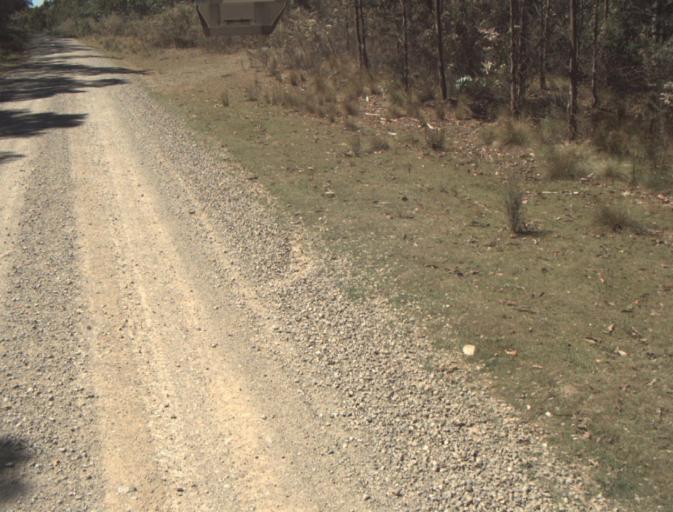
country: AU
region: Tasmania
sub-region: Dorset
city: Scottsdale
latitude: -41.3033
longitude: 147.4687
